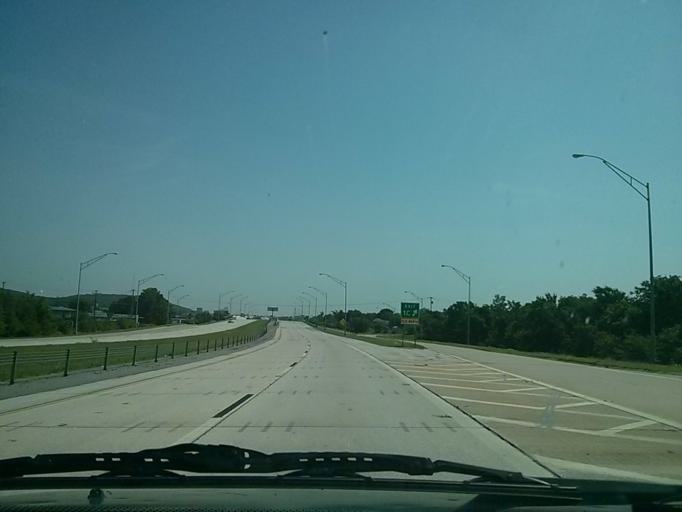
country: US
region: Oklahoma
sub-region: Tulsa County
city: Oakhurst
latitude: 36.0952
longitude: -96.0322
